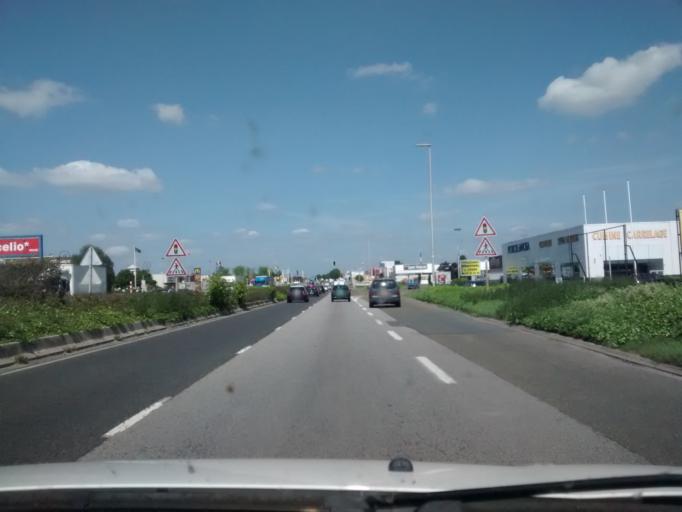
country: FR
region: Ile-de-France
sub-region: Departement des Yvelines
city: Coignieres
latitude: 48.7475
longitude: 1.9231
